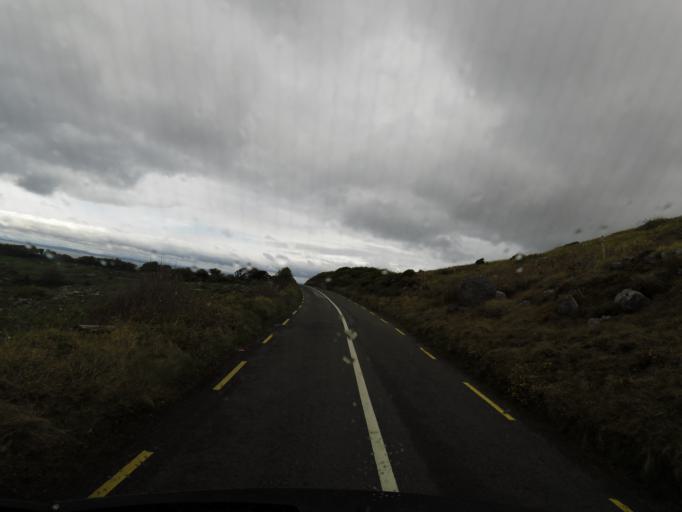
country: IE
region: Connaught
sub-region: County Galway
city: Bearna
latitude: 53.1369
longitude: -9.2754
